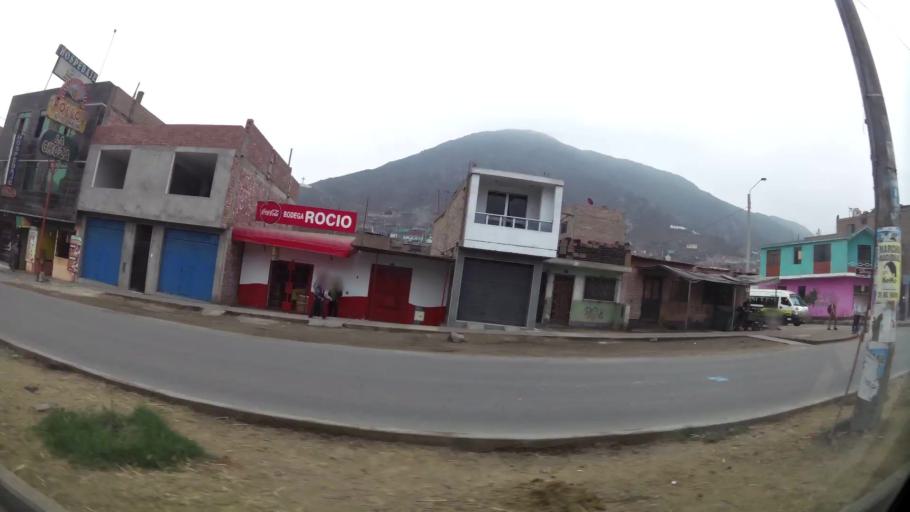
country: PE
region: Lima
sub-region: Lima
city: Urb. Santo Domingo
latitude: -11.9141
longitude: -77.0283
